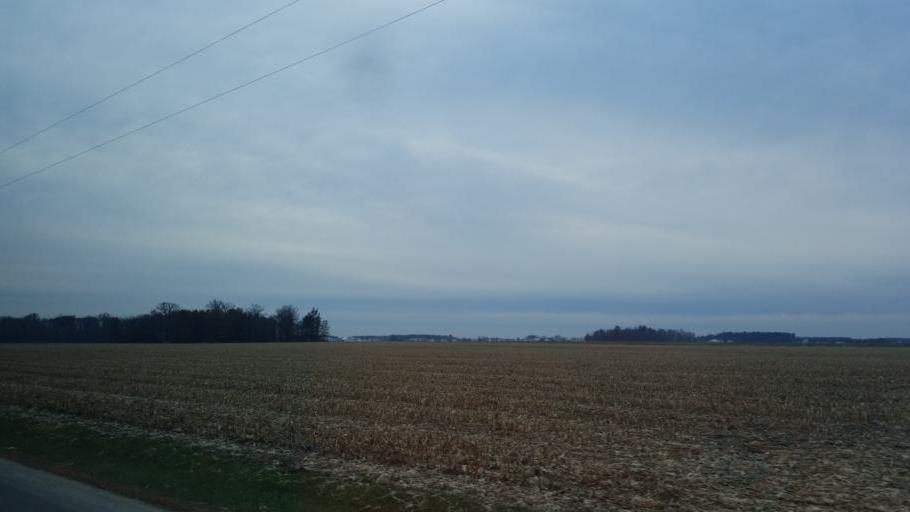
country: US
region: Indiana
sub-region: Adams County
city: Berne
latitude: 40.7313
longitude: -84.8797
